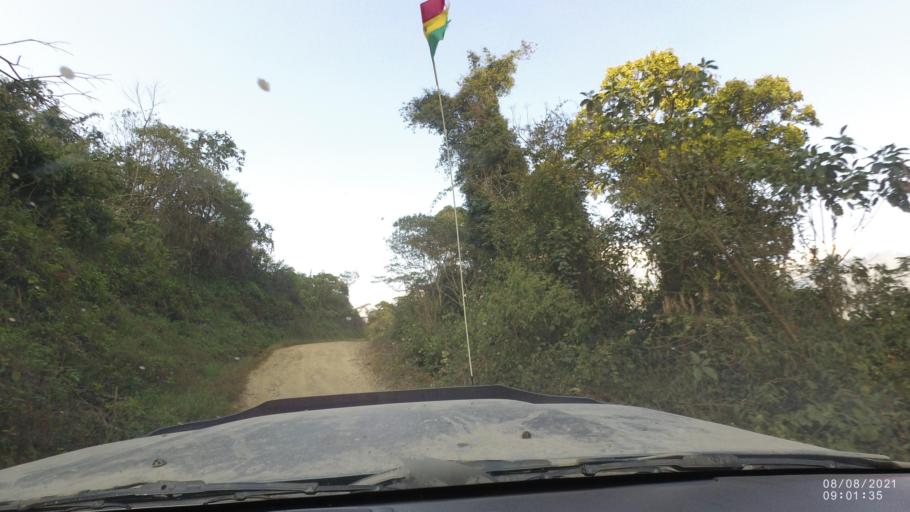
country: BO
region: La Paz
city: Quime
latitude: -16.5505
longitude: -66.7370
